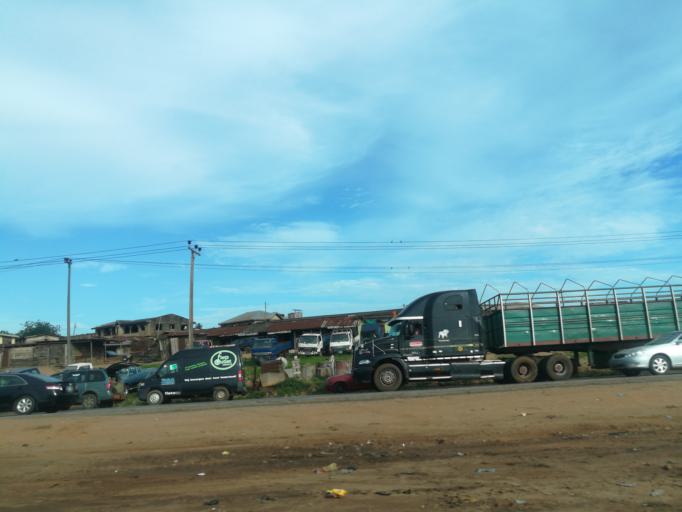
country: NG
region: Oyo
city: Ibadan
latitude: 7.3529
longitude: 3.9194
